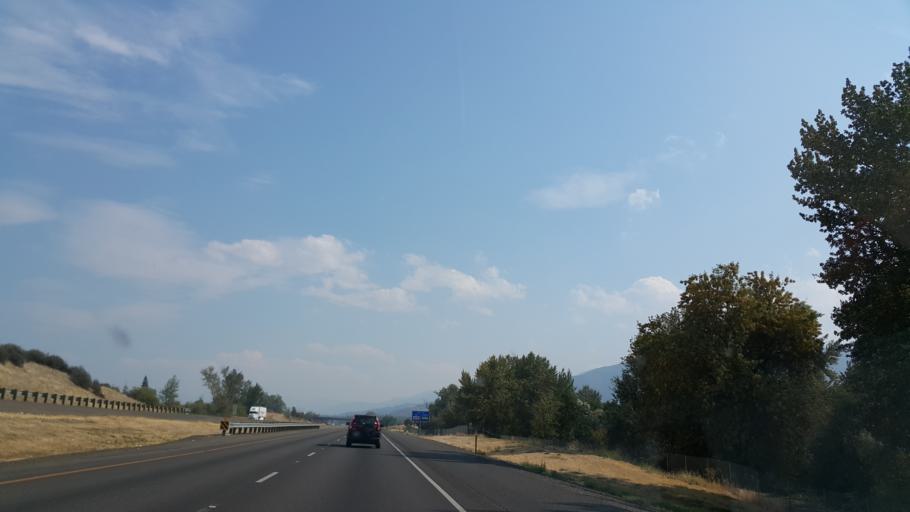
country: US
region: Oregon
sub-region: Jackson County
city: Talent
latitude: 42.2513
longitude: -122.7810
